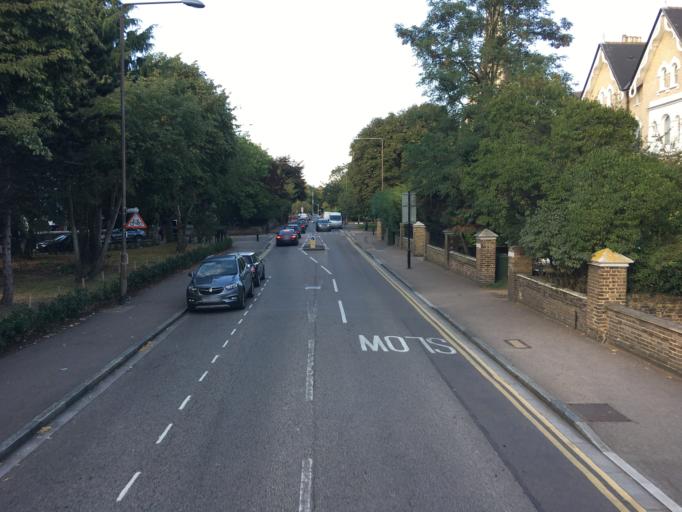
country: GB
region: England
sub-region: Greater London
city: Blackheath
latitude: 51.4752
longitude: 0.0174
